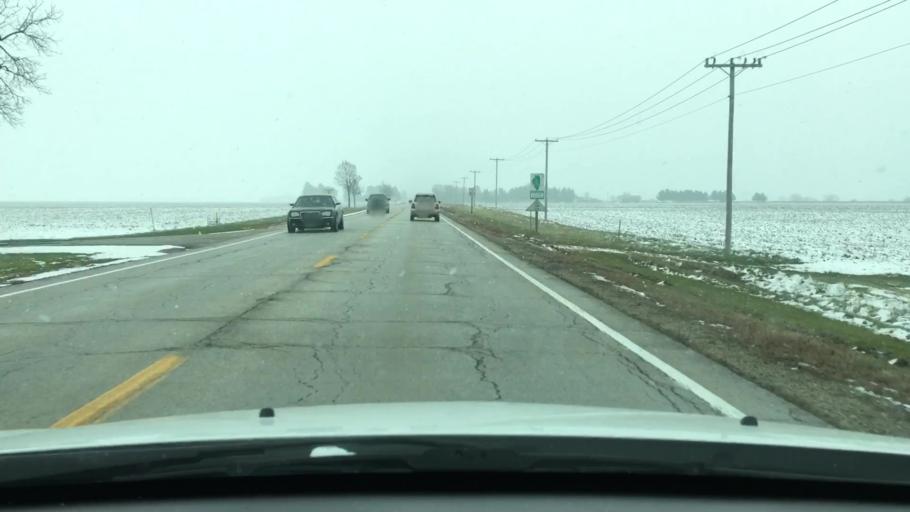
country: US
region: Illinois
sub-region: DeKalb County
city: Malta
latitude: 41.9357
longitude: -88.8567
